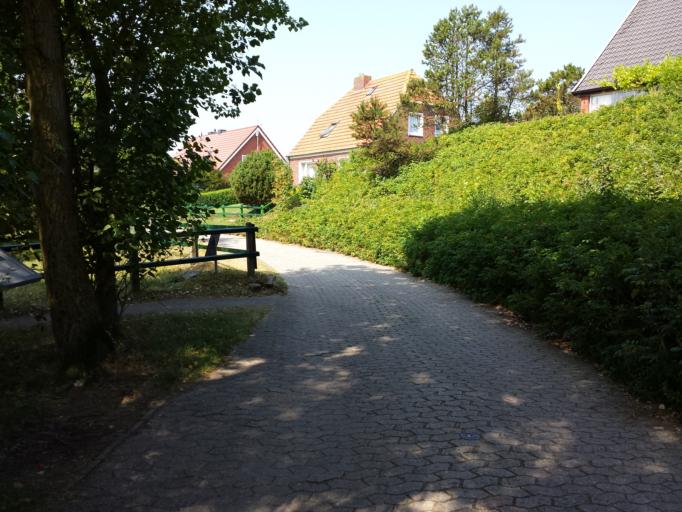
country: DE
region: Lower Saxony
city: Spiekeroog
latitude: 53.7718
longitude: 7.7006
